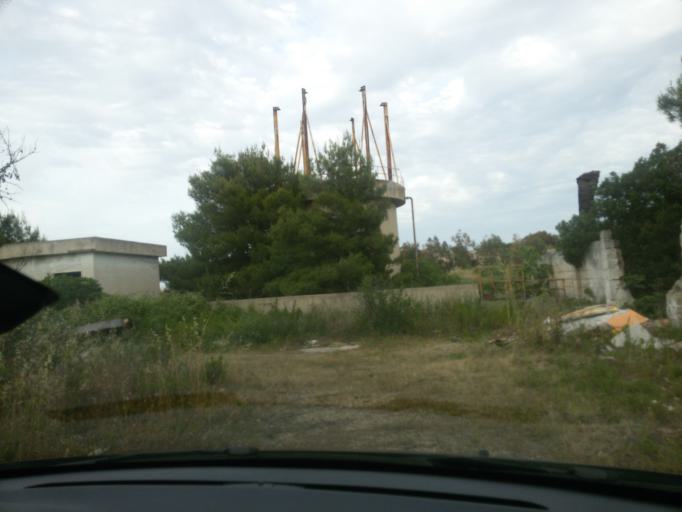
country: IT
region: Apulia
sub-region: Provincia di Brindisi
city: Materdomini
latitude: 40.6589
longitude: 17.9548
